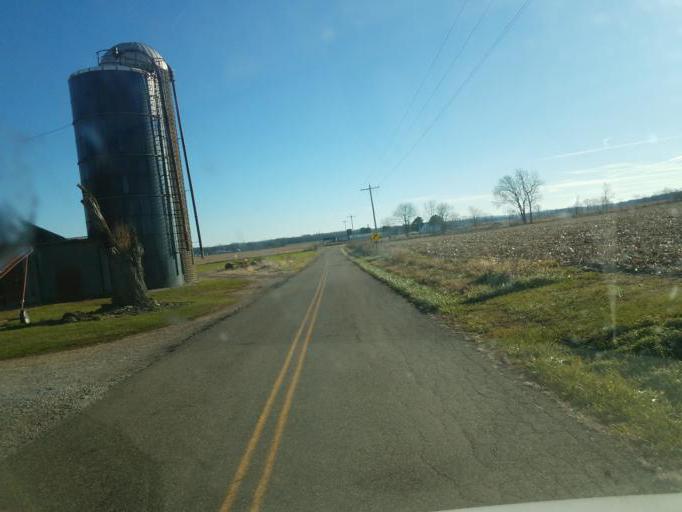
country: US
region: Ohio
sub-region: Knox County
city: Fredericktown
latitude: 40.4486
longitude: -82.5663
